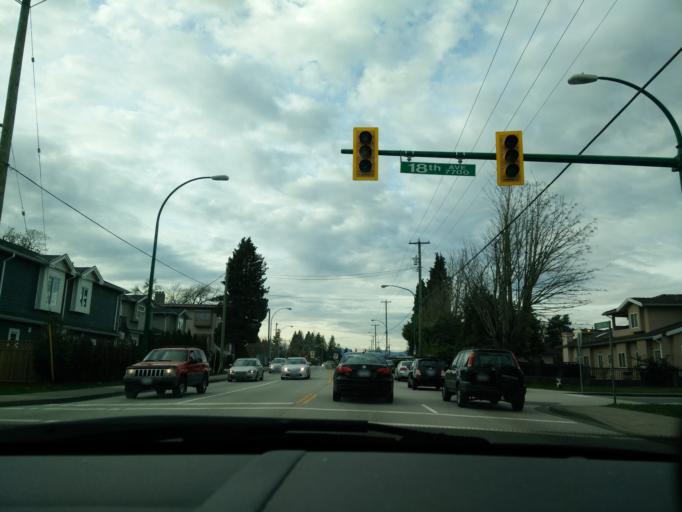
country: CA
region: British Columbia
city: New Westminster
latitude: 49.2228
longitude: -122.9392
